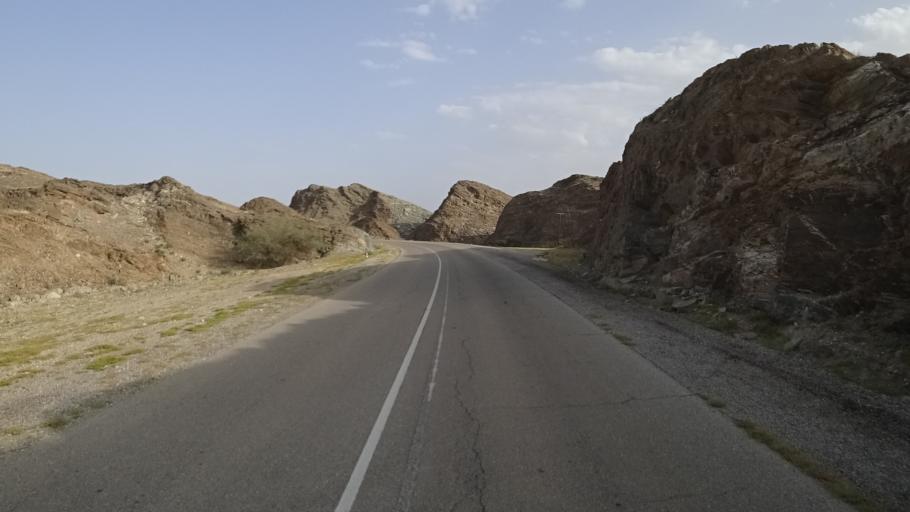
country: OM
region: Muhafazat Masqat
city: Bawshar
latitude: 23.3600
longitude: 58.5259
